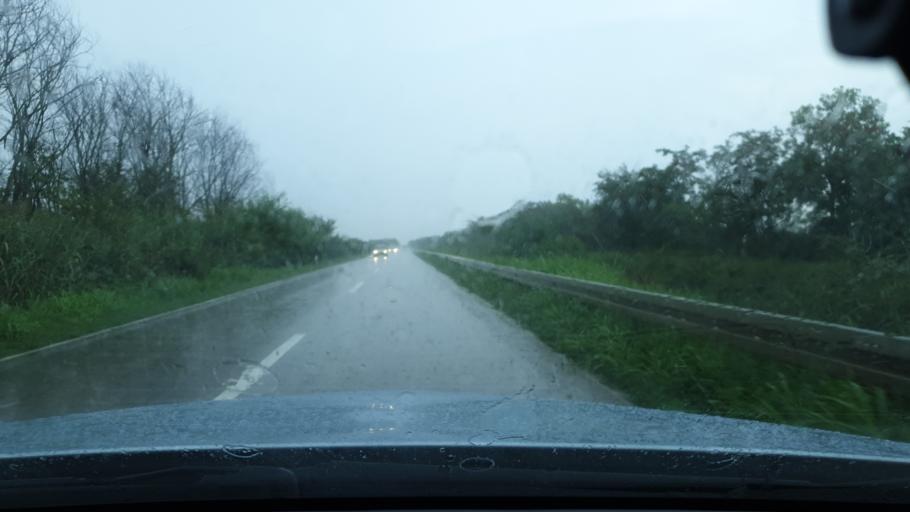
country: RS
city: Lazarevo
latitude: 45.3893
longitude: 20.5877
